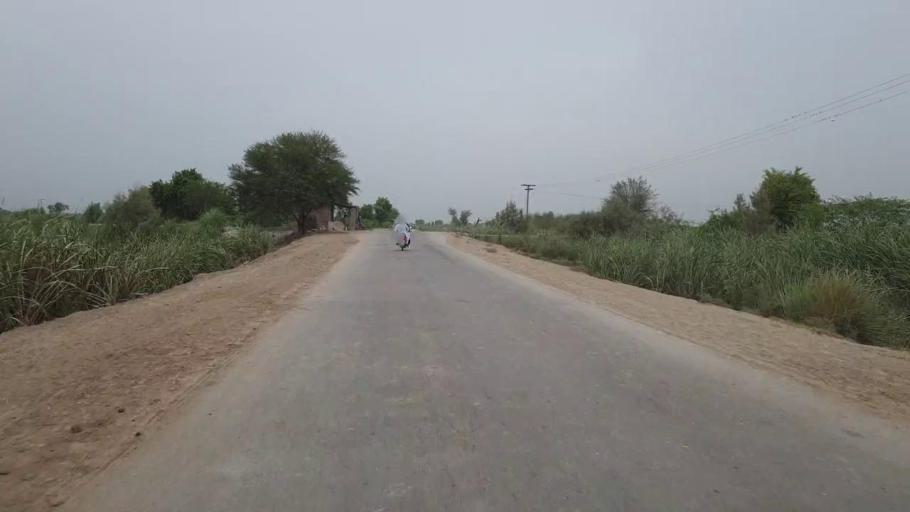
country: PK
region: Sindh
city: Bandhi
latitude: 26.5546
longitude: 68.2099
